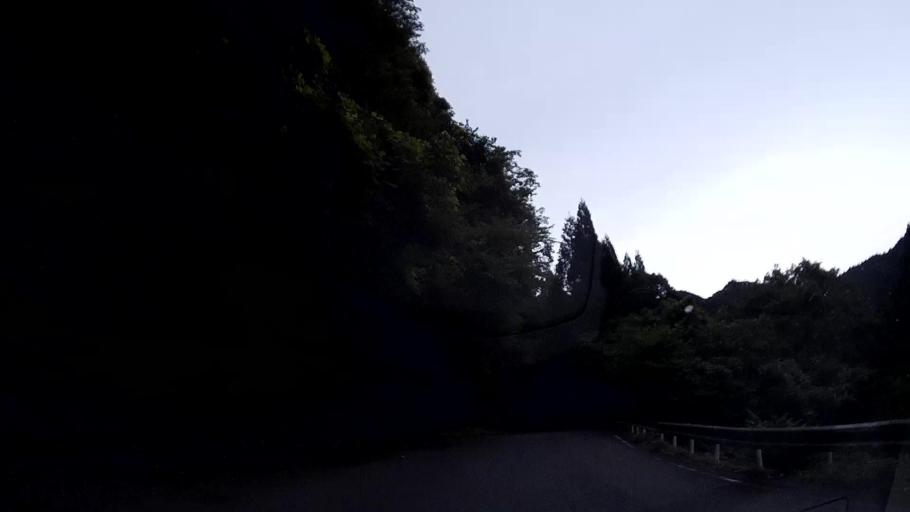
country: JP
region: Kumamoto
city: Kikuchi
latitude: 33.0957
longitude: 130.9565
